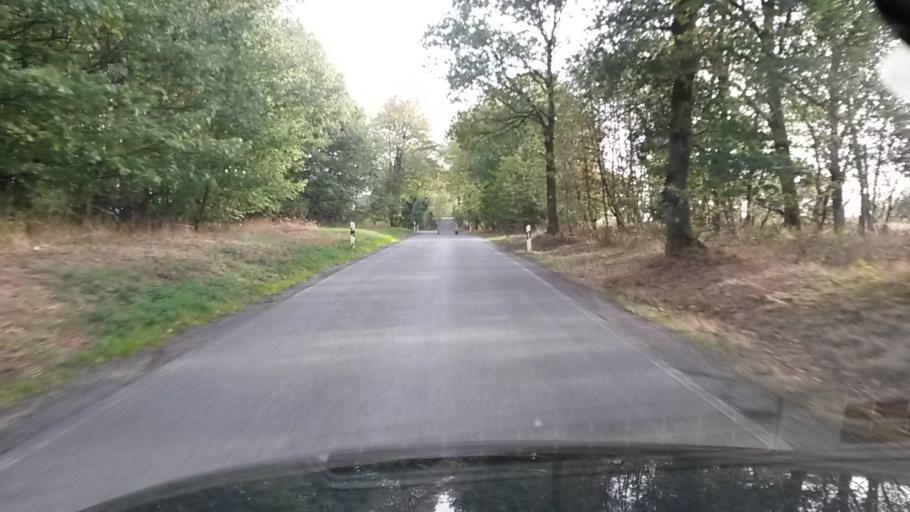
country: DE
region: North Rhine-Westphalia
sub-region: Regierungsbezirk Arnsberg
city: Herscheid
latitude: 51.1877
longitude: 7.7497
